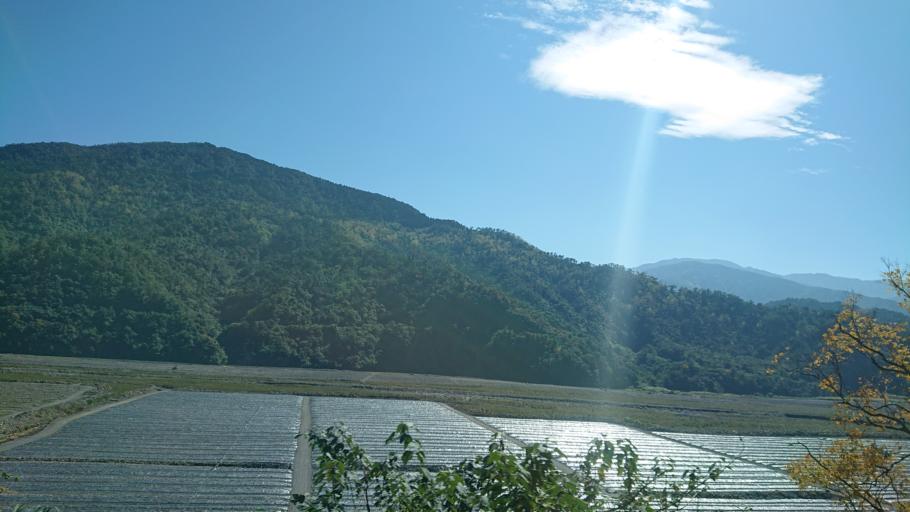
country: TW
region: Taiwan
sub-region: Yilan
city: Yilan
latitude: 24.5878
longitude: 121.5034
